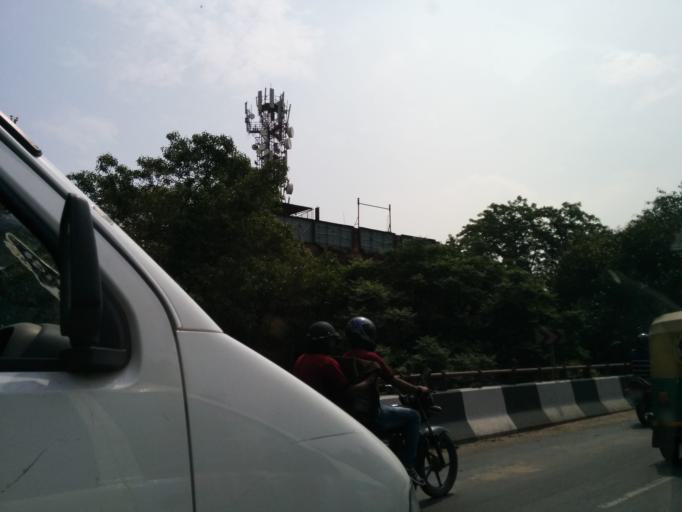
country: IN
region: NCT
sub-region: New Delhi
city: New Delhi
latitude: 28.5450
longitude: 77.2004
